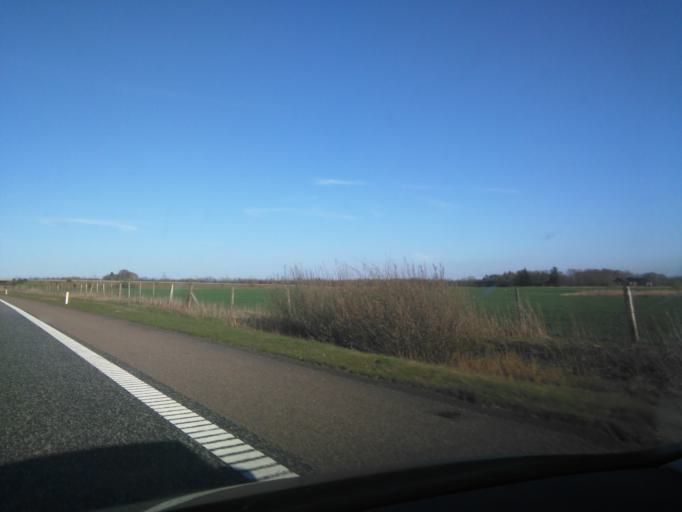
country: DK
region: Central Jutland
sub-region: Herning Kommune
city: Hammerum
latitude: 56.1206
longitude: 9.0692
